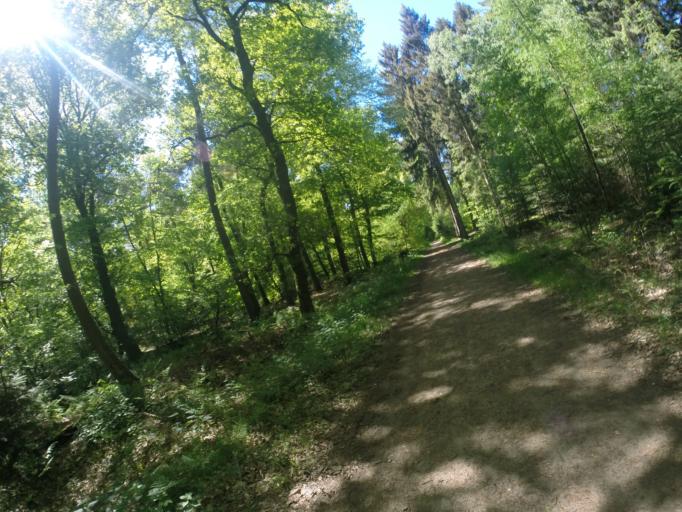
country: NL
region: Gelderland
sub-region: Gemeente Montferland
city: s-Heerenberg
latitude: 51.9125
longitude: 6.2317
